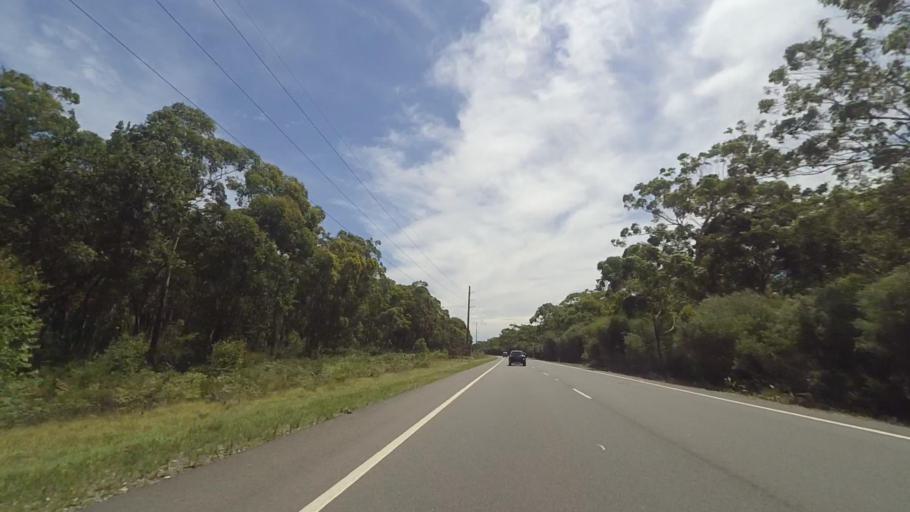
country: AU
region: New South Wales
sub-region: Port Stephens Shire
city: Anna Bay
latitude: -32.7817
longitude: 151.9871
